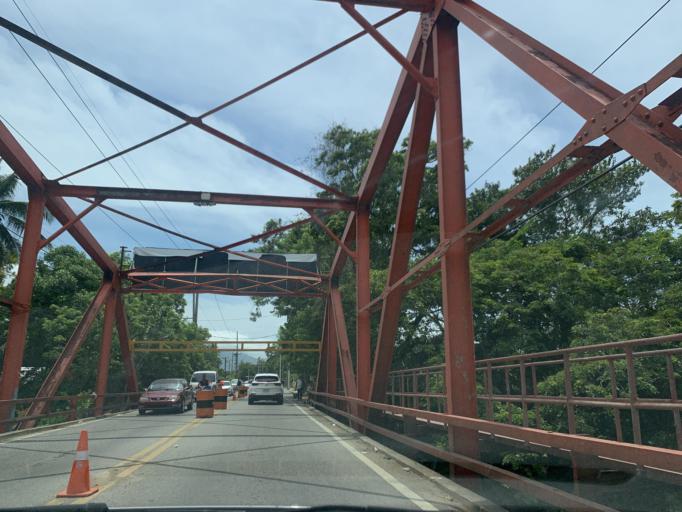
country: DO
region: Puerto Plata
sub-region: Puerto Plata
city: Puerto Plata
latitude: 19.7478
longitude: -70.5917
